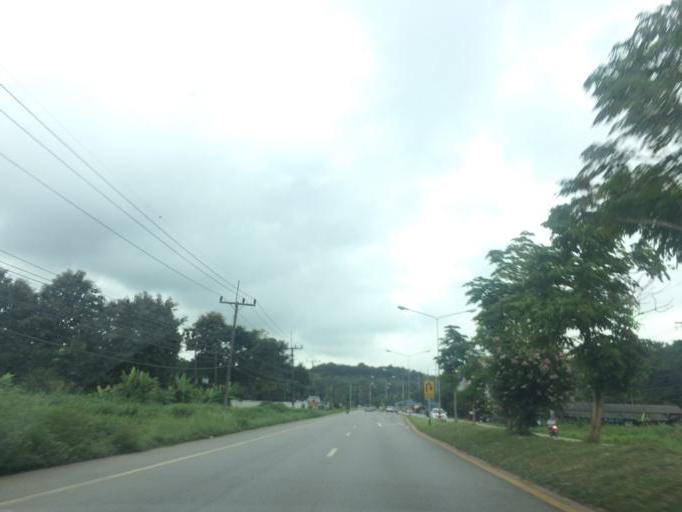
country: TH
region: Chiang Rai
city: Mae Chan
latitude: 20.1118
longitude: 99.8732
